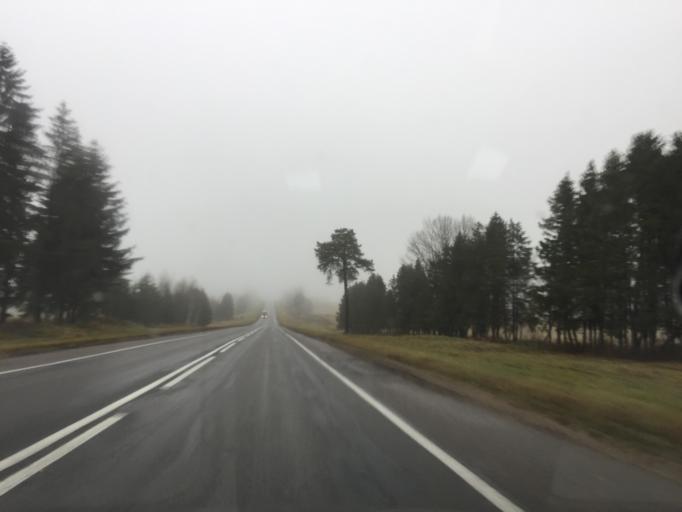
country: BY
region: Mogilev
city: Kamyennyya Lavy
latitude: 54.1512
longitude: 30.4564
